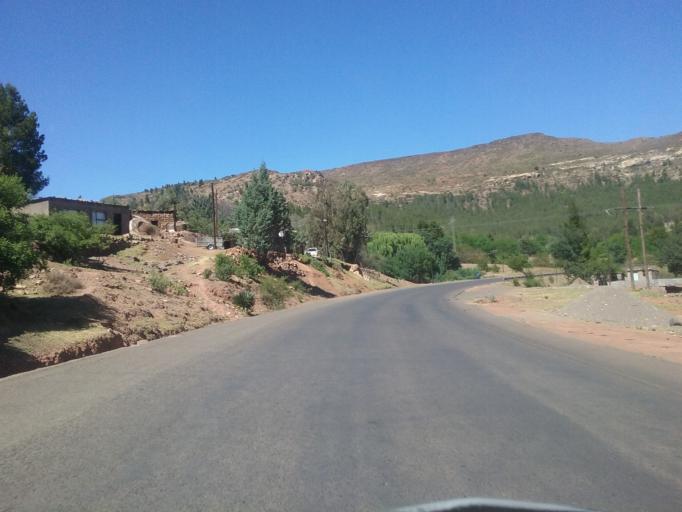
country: LS
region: Quthing
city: Quthing
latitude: -30.4023
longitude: 27.6844
